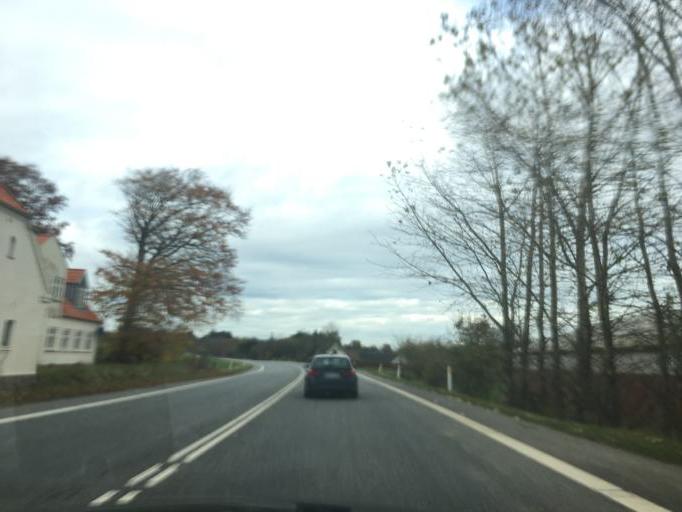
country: DK
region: South Denmark
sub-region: Vejle Kommune
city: Vejle
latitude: 55.6621
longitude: 9.5116
